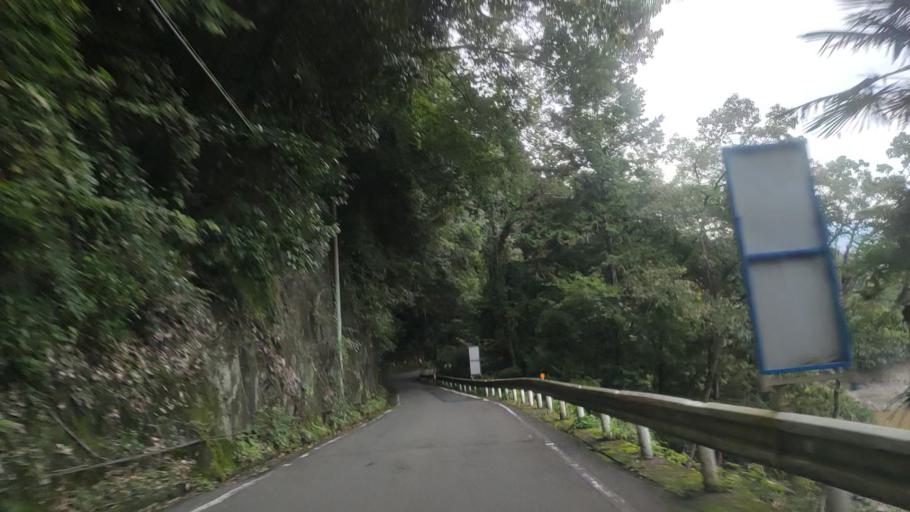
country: JP
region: Wakayama
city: Hashimoto
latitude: 34.3085
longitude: 135.6227
